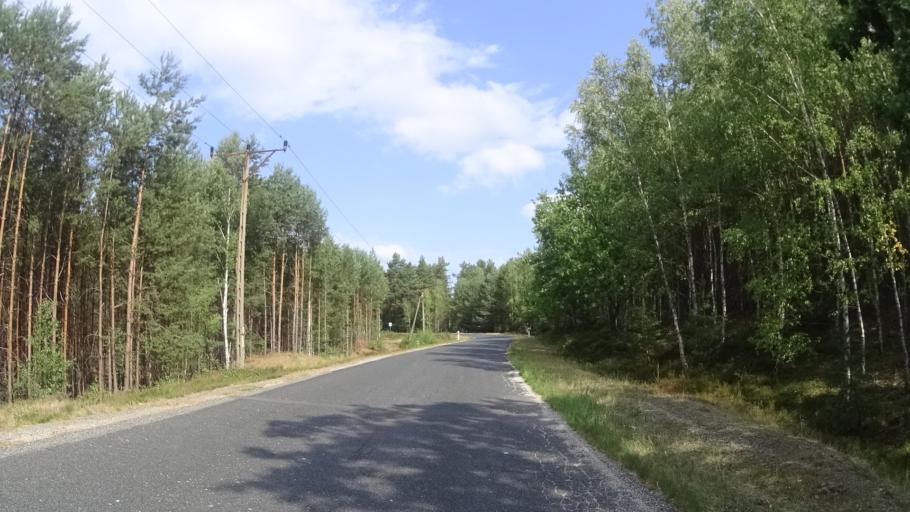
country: PL
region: Lubusz
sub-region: Powiat zarski
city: Leknica
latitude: 51.5276
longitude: 14.8193
